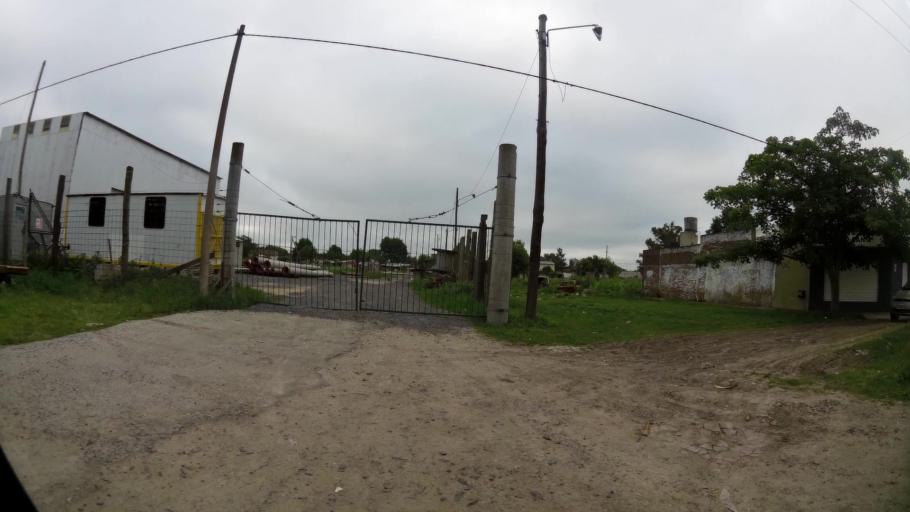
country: AR
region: Buenos Aires
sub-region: Partido de La Plata
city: La Plata
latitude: -34.9328
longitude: -57.9919
